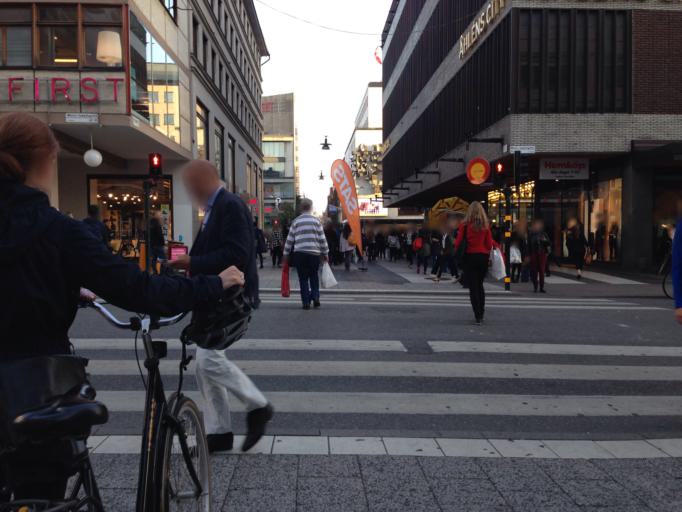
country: SE
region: Stockholm
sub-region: Stockholms Kommun
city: Stockholm
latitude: 59.3330
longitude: 18.0623
